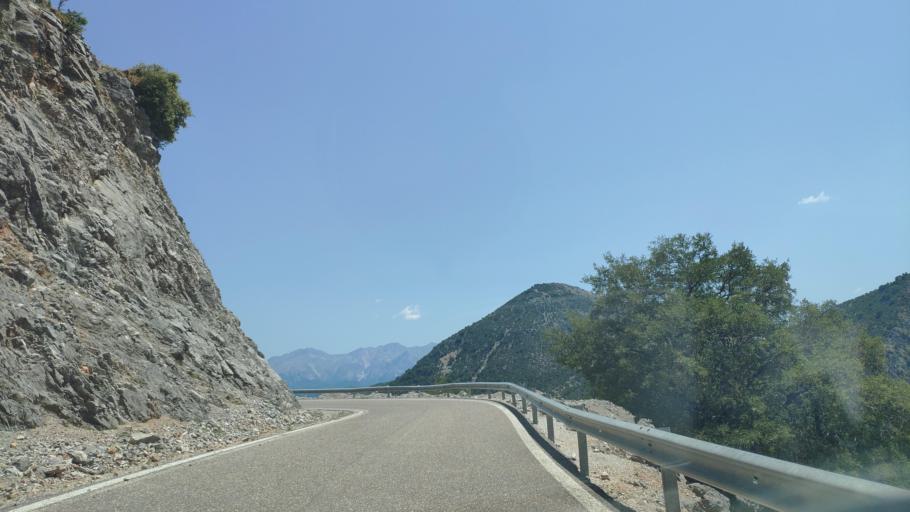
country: GR
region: West Greece
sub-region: Nomos Aitolias kai Akarnanias
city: Krikellos
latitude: 39.0223
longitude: 21.3701
